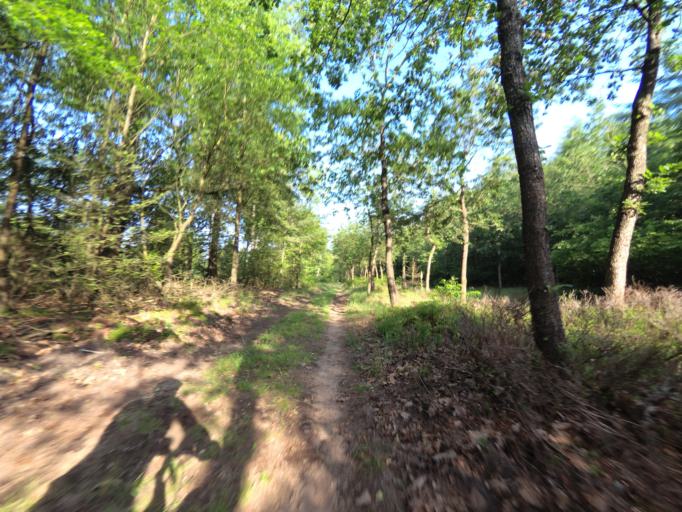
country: NL
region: Gelderland
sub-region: Gemeente Apeldoorn
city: Beekbergen
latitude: 52.1529
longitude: 5.8919
